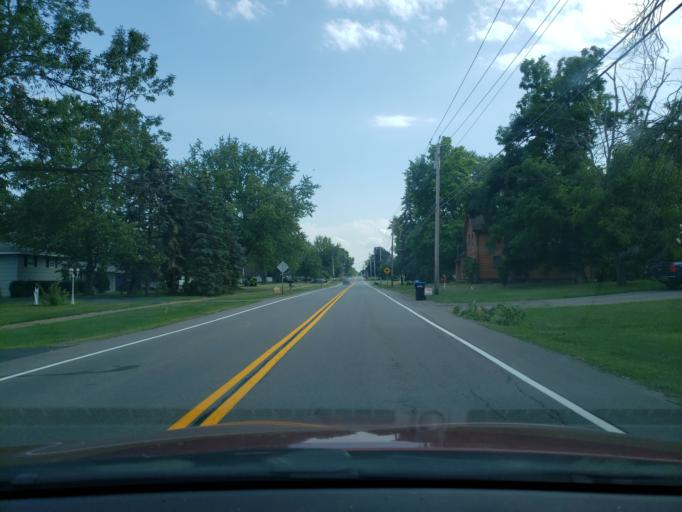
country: US
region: New York
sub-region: Monroe County
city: Greece
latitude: 43.2748
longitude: -77.7149
